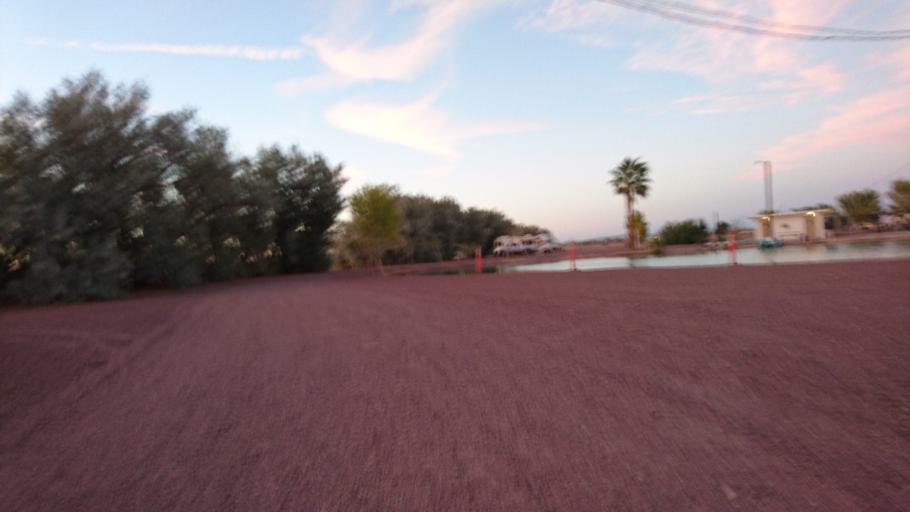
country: US
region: California
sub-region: San Bernardino County
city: Barstow
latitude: 34.8153
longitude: -116.6166
